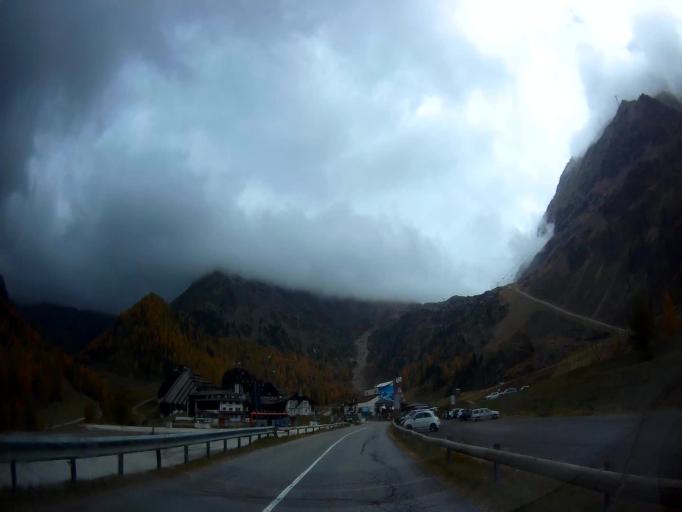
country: IT
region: Trentino-Alto Adige
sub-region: Bolzano
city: Silandro
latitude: 46.7552
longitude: 10.7836
